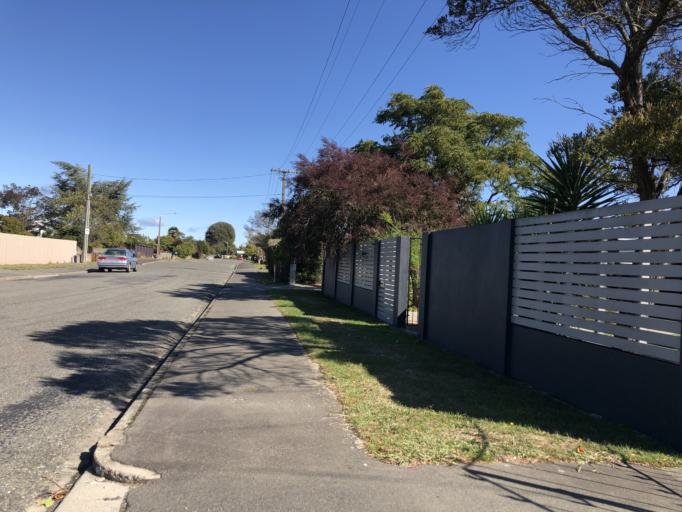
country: NZ
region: Tasman
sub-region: Tasman District
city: Richmond
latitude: -41.3407
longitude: 173.1771
